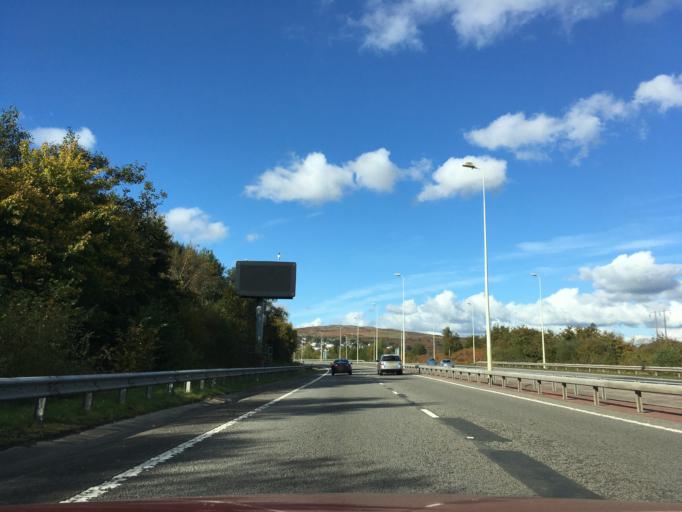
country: GB
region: Wales
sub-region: Merthyr Tydfil County Borough
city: Merthyr Tydfil
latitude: 51.7528
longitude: -3.3985
